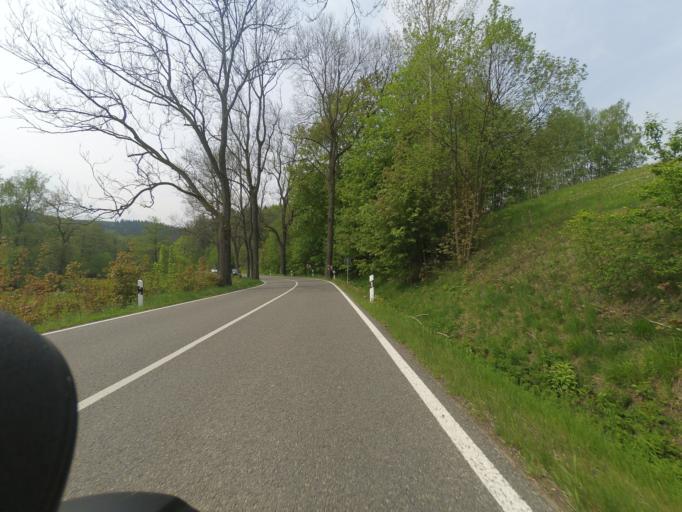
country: DE
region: Saxony
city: Pfaffroda
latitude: 50.6936
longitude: 13.3483
